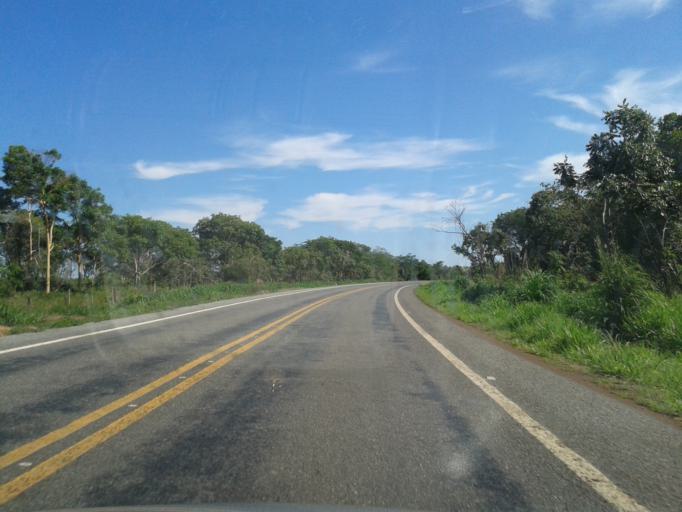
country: BR
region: Goias
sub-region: Piracanjuba
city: Piracanjuba
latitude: -17.2948
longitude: -48.7904
